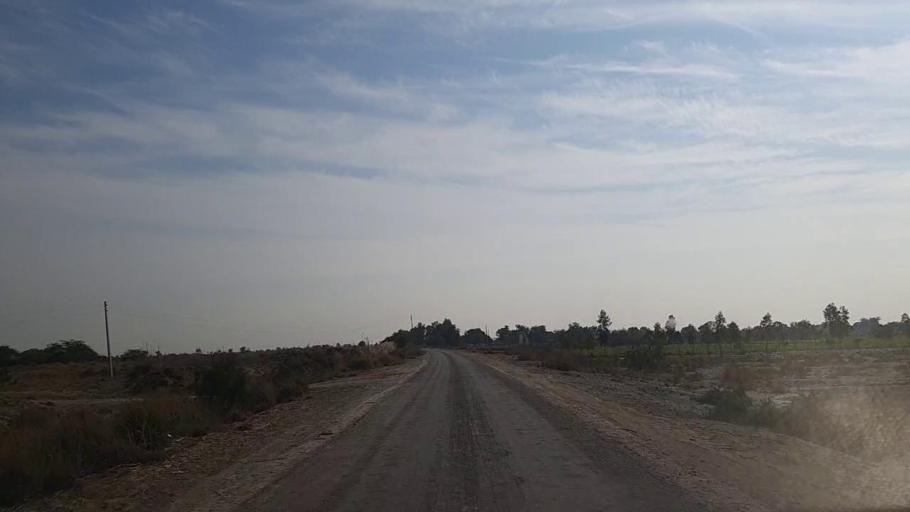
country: PK
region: Sindh
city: Daur
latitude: 26.4746
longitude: 68.4178
